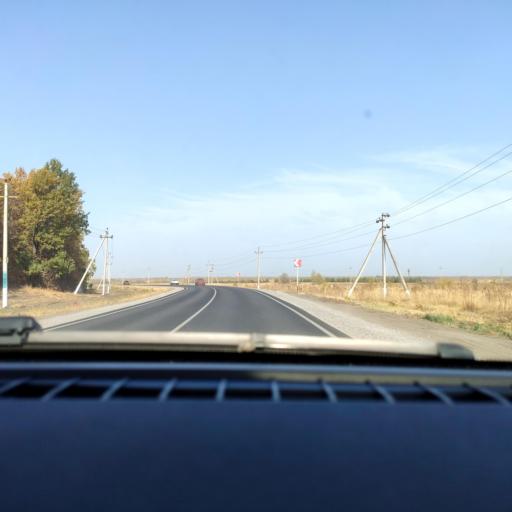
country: RU
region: Voronezj
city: Novaya Usman'
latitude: 51.6867
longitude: 39.3970
